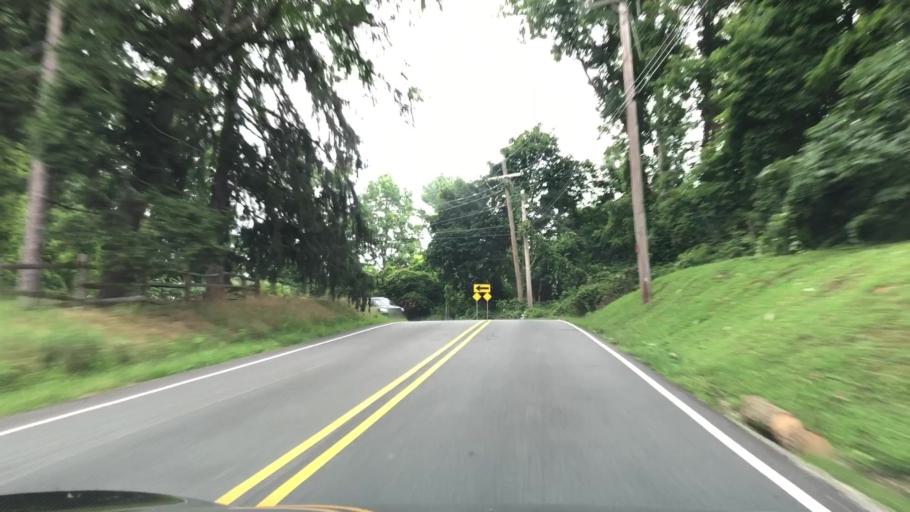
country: US
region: Pennsylvania
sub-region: Chester County
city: Devon
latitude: 40.0253
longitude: -75.4180
